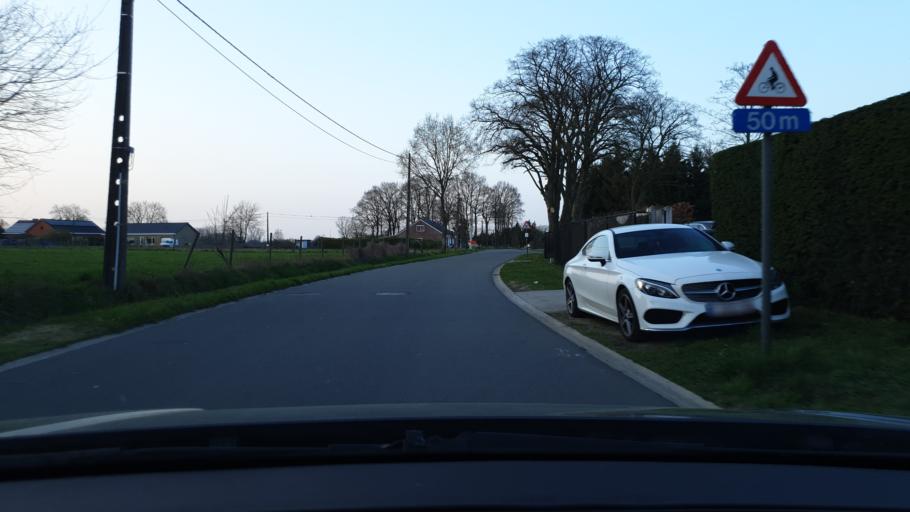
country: BE
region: Flanders
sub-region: Provincie Antwerpen
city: Geel
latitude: 51.1363
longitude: 4.9894
